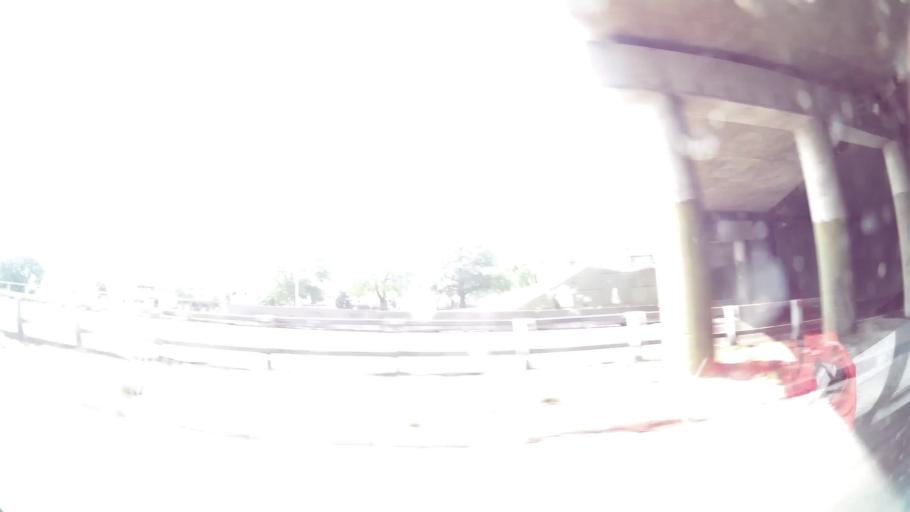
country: AR
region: Buenos Aires F.D.
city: Villa Lugano
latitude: -34.6498
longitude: -58.4659
